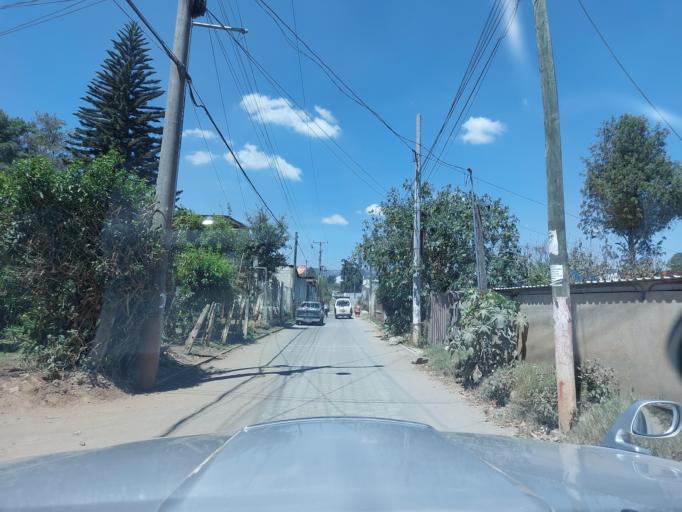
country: GT
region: Chimaltenango
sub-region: Municipio de Chimaltenango
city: Chimaltenango
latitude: 14.6561
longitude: -90.8283
